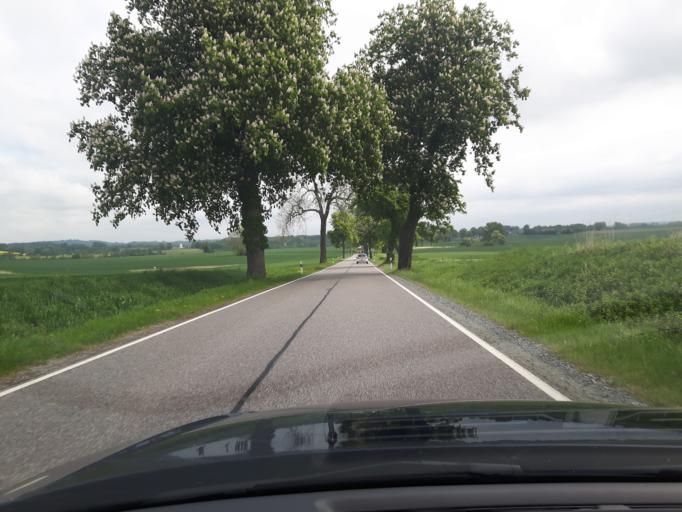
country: DE
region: Mecklenburg-Vorpommern
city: Gross Wokern
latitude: 53.6586
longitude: 12.5072
